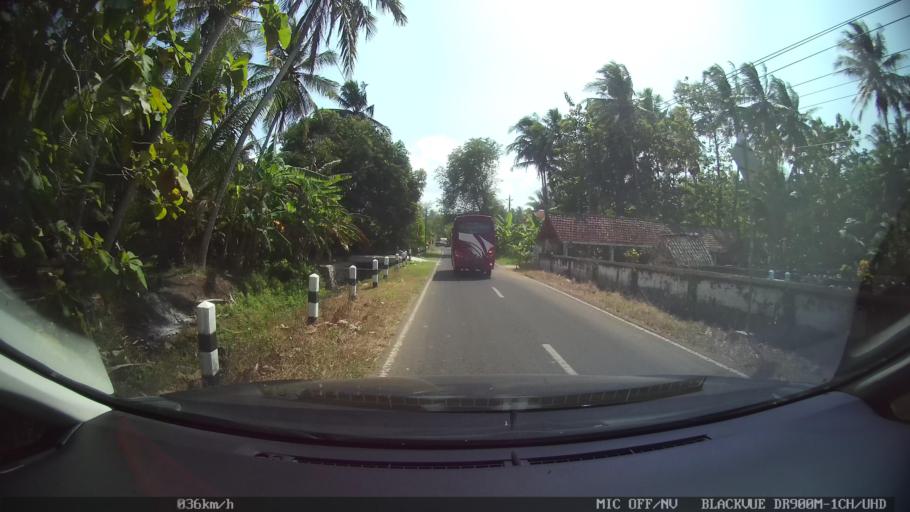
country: ID
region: Daerah Istimewa Yogyakarta
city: Srandakan
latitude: -7.9251
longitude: 110.1570
